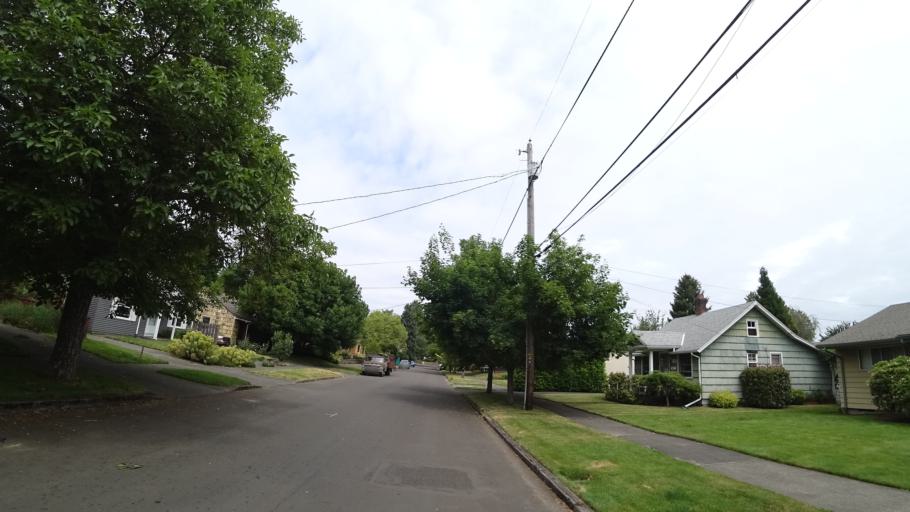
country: US
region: Oregon
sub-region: Multnomah County
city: Portland
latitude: 45.5685
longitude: -122.6276
